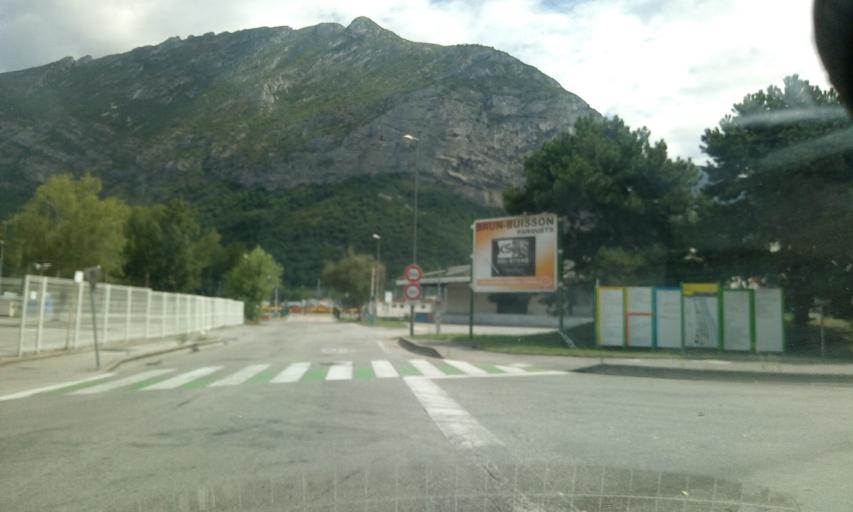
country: FR
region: Rhone-Alpes
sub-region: Departement de l'Isere
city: Fontaine
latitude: 45.2150
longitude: 5.6860
